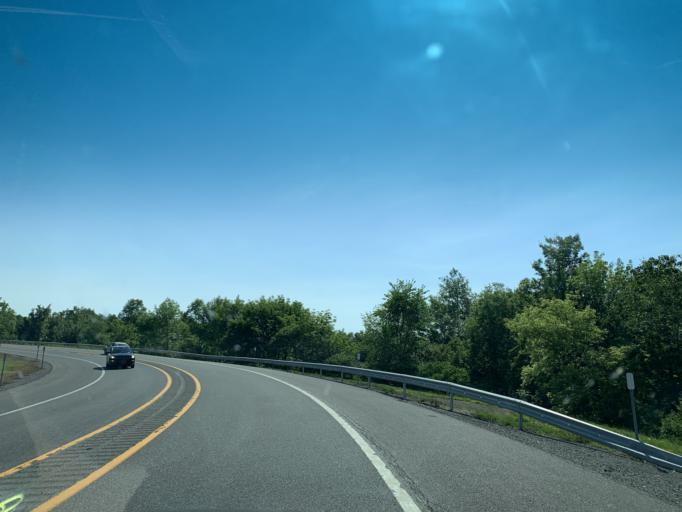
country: US
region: New York
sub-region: Oneida County
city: Sherrill
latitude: 43.1258
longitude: -75.5818
